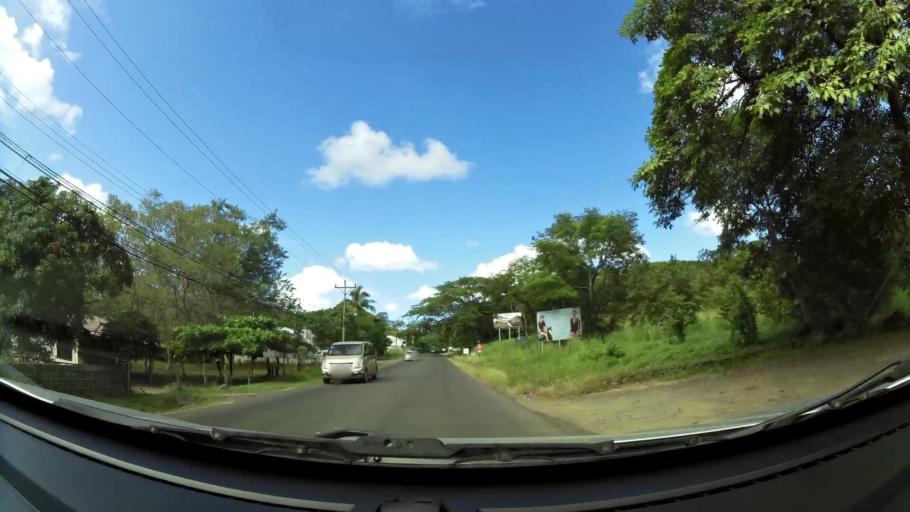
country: CR
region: Guanacaste
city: Santa Cruz
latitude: 10.3088
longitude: -85.8097
